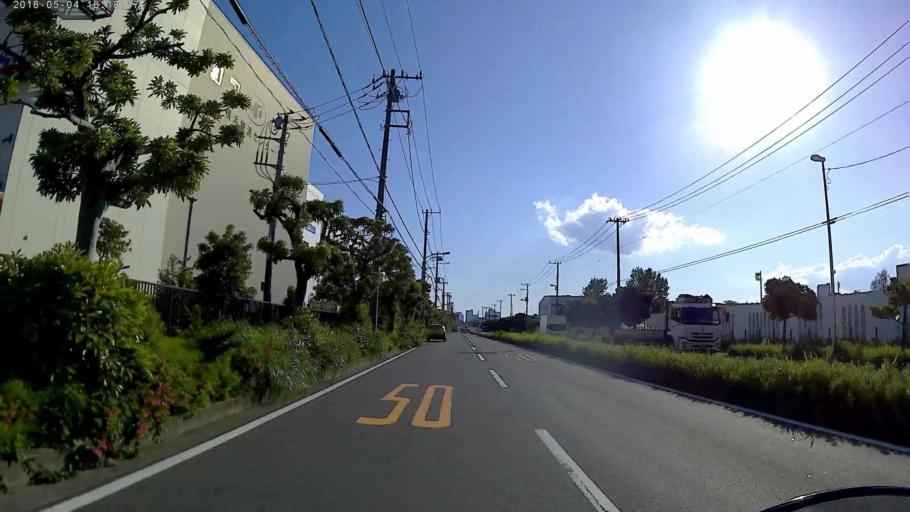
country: JP
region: Kanagawa
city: Yokohama
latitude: 35.4853
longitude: 139.6705
